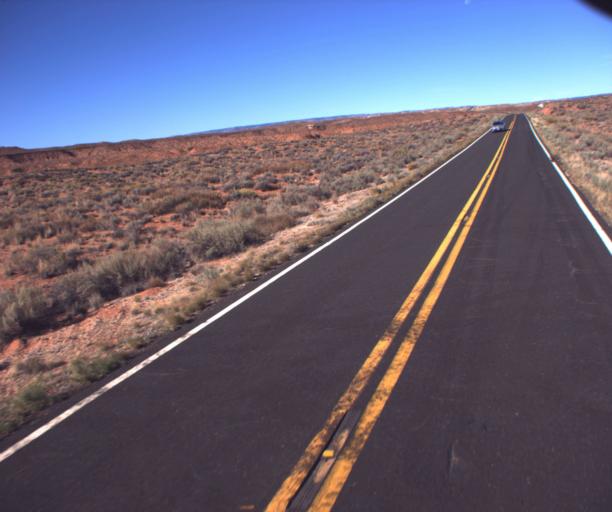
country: US
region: Arizona
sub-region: Coconino County
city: Page
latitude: 36.6878
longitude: -111.8705
